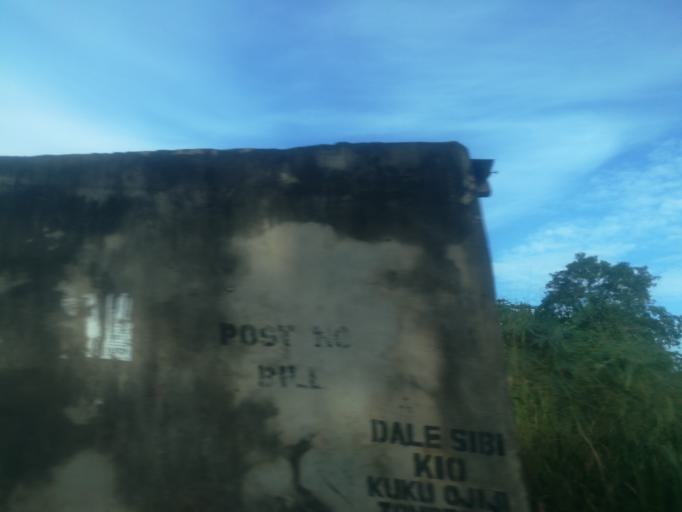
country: NG
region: Oyo
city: Ibadan
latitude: 7.3421
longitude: 3.8900
